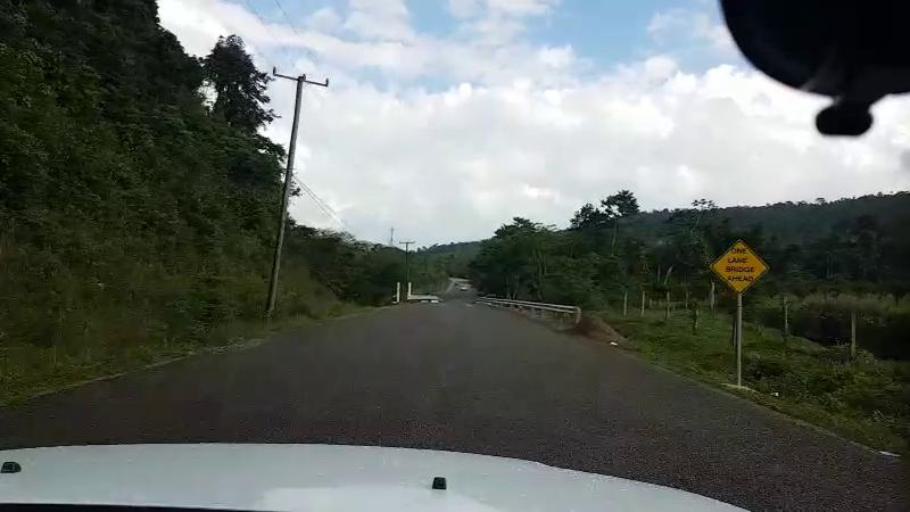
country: BZ
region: Cayo
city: Belmopan
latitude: 17.0900
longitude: -88.6212
